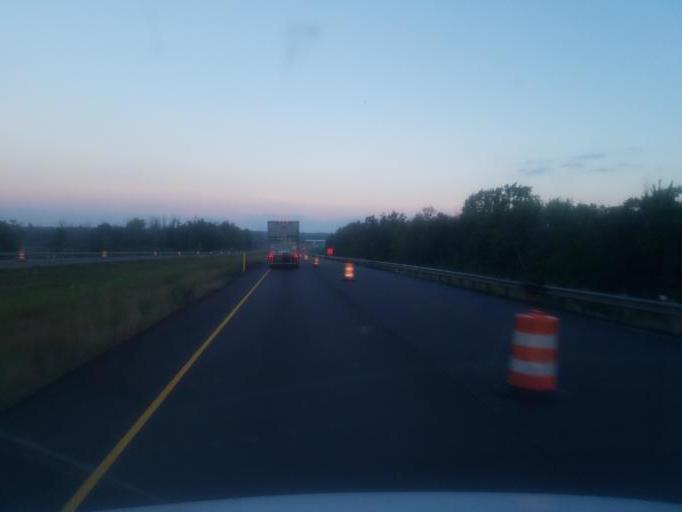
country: US
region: Ohio
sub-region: Ashtabula County
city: Jefferson
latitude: 41.8019
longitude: -80.7504
